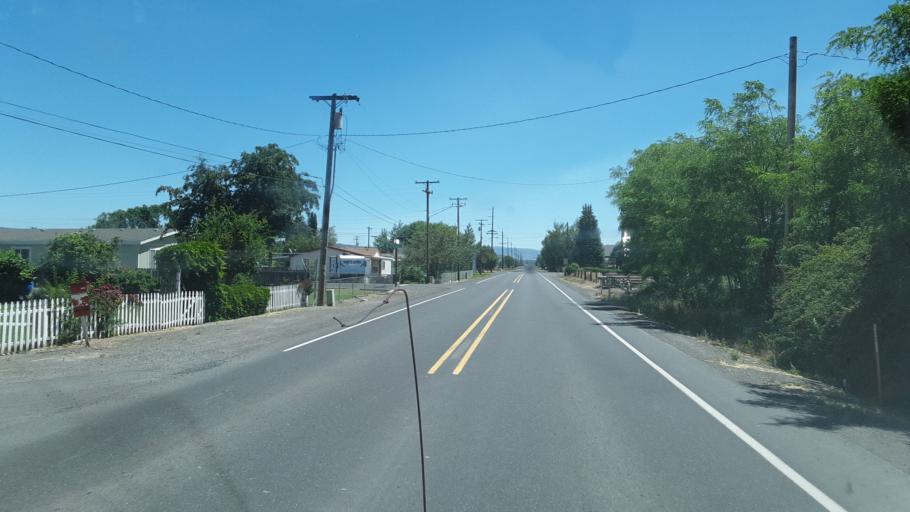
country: US
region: California
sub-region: Siskiyou County
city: Tulelake
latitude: 42.0239
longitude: -121.5930
